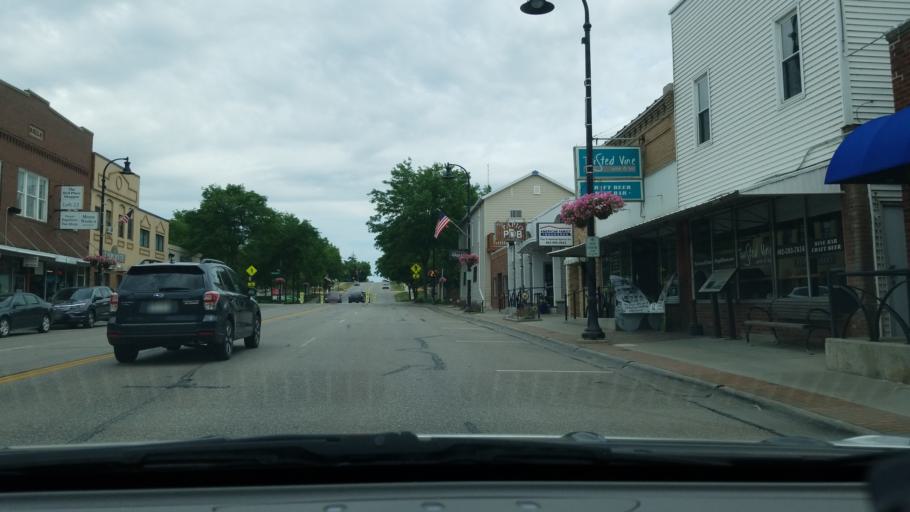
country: US
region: Nebraska
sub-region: Sarpy County
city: Papillion
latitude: 41.1567
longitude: -96.0429
